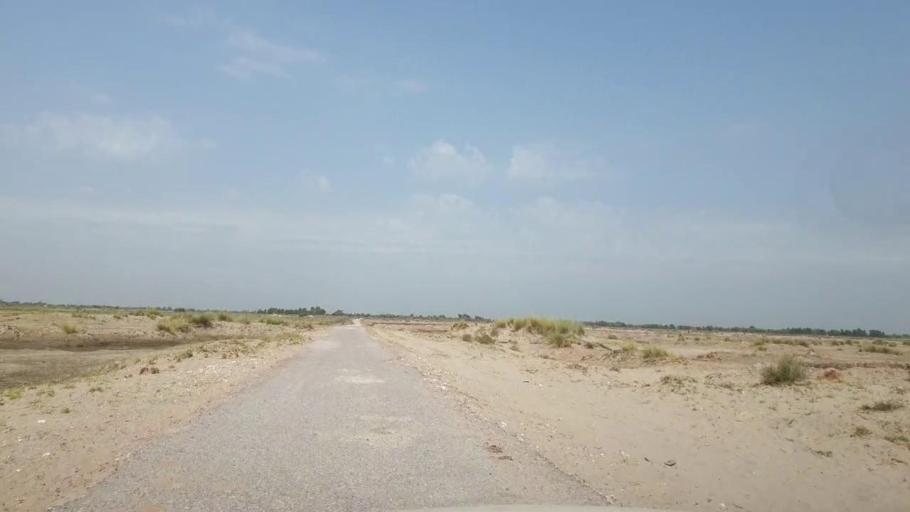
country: PK
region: Sindh
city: Ratodero
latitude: 27.8386
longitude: 68.2586
